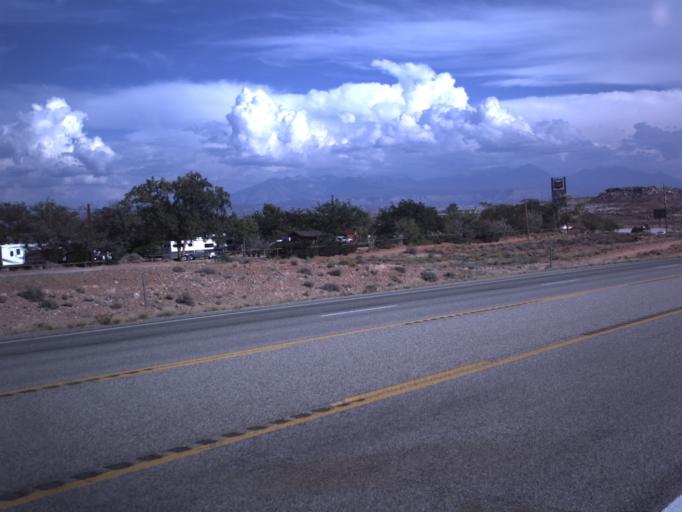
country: US
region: Utah
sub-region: Grand County
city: Moab
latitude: 38.6782
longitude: -109.6907
